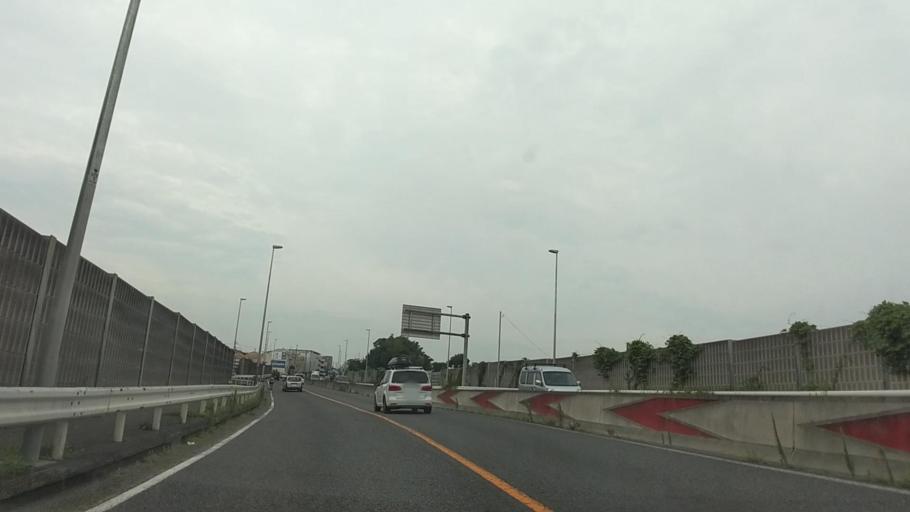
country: JP
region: Kanagawa
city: Fujisawa
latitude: 35.4113
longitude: 139.5315
